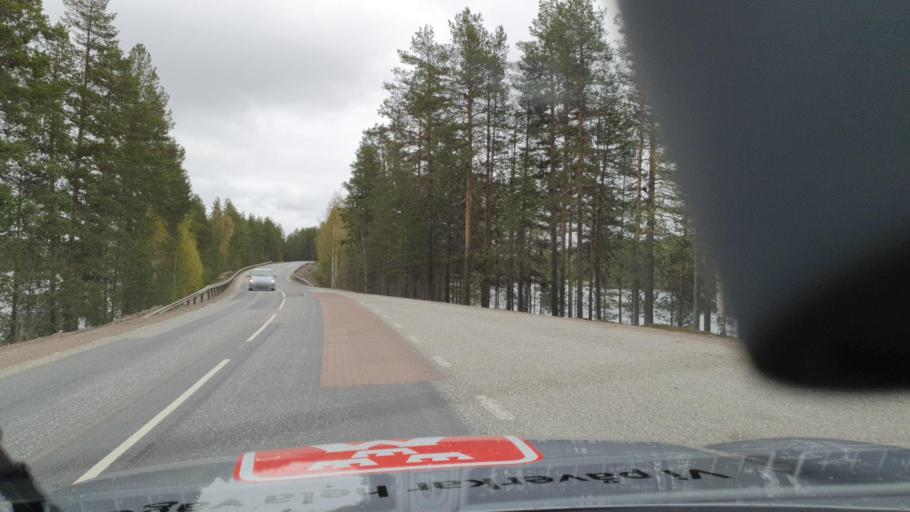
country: SE
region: Vaesternorrland
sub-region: Solleftea Kommun
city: Solleftea
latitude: 63.6481
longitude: 17.3773
